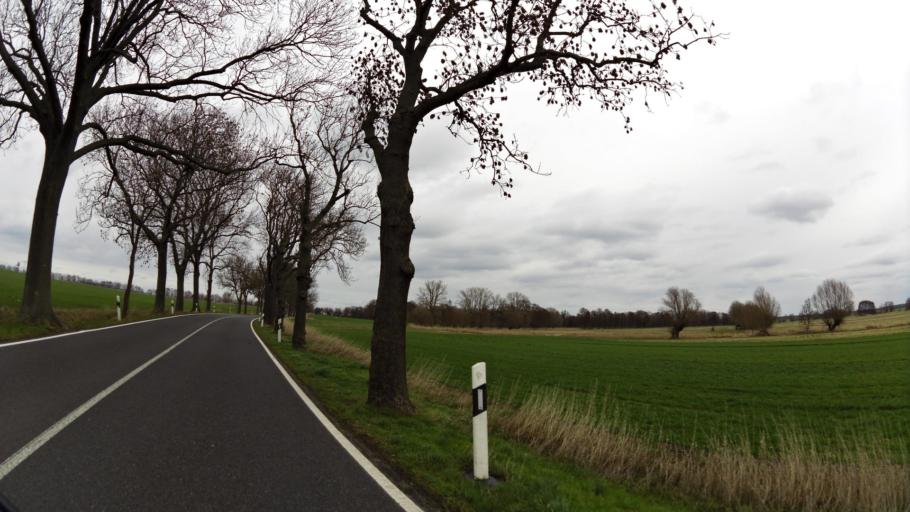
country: DE
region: Brandenburg
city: Schonefeld
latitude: 52.3367
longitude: 13.5018
